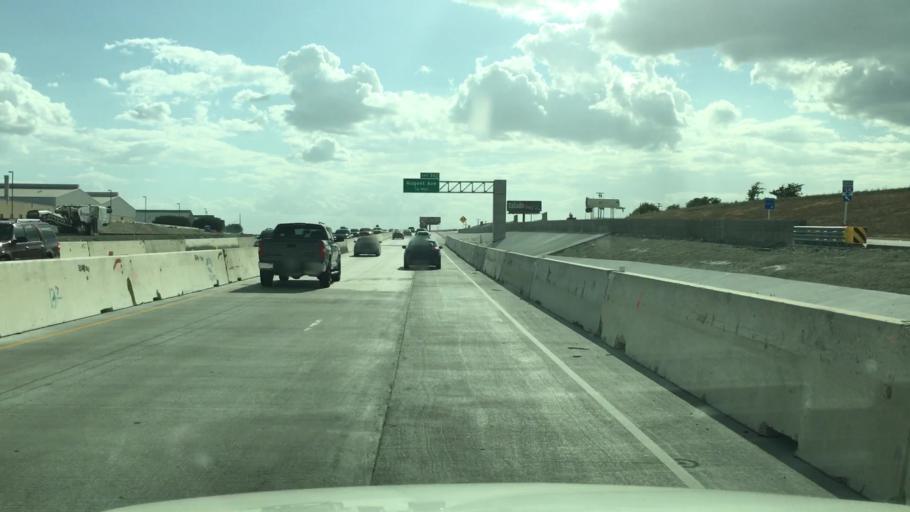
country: US
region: Texas
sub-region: Bell County
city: Temple
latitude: 31.1250
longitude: -97.3433
